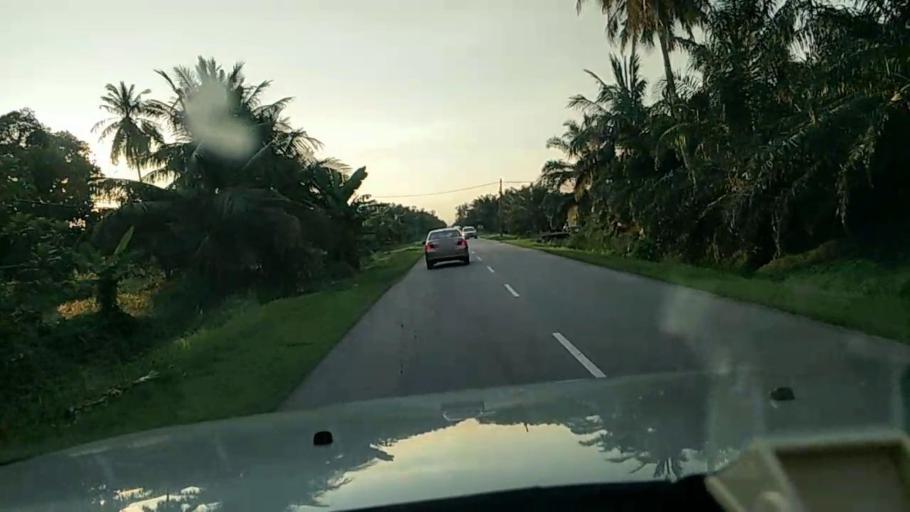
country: MY
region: Selangor
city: Kuala Selangor
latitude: 3.3118
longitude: 101.2868
